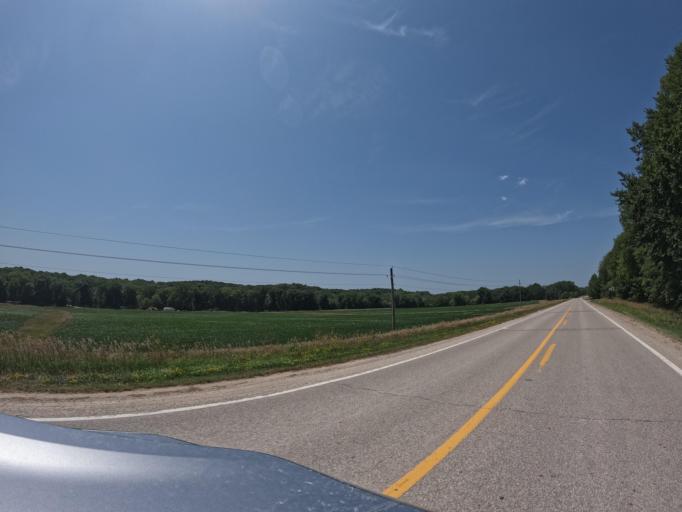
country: US
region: Iowa
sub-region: Henry County
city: Mount Pleasant
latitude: 40.9369
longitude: -91.6078
